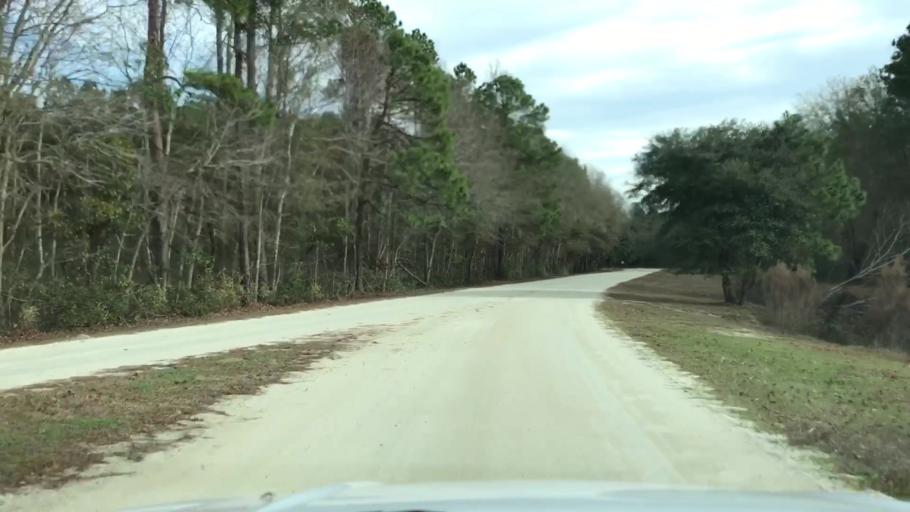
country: US
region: South Carolina
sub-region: Charleston County
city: Isle of Palms
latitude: 32.9049
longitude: -79.7220
